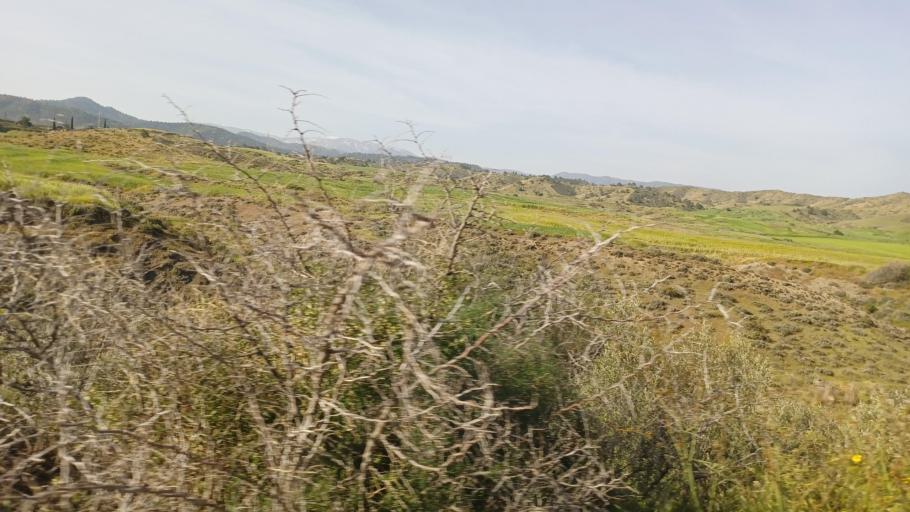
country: CY
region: Lefkosia
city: Astromeritis
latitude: 35.0877
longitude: 32.9506
